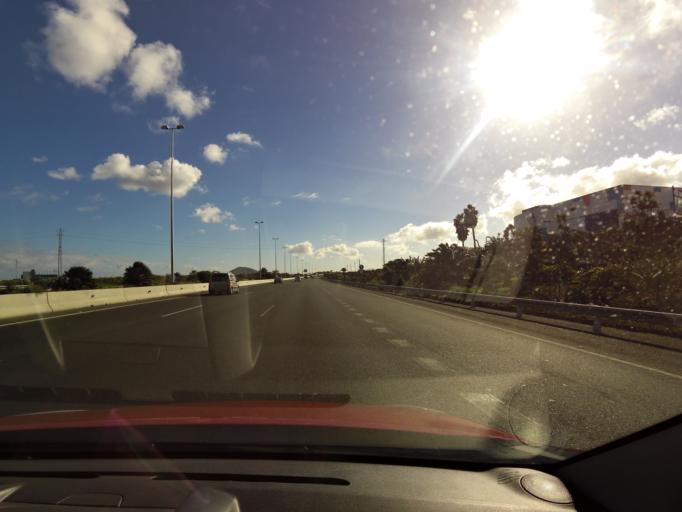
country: ES
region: Canary Islands
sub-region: Provincia de Las Palmas
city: Ingenio
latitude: 27.9168
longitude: -15.3984
